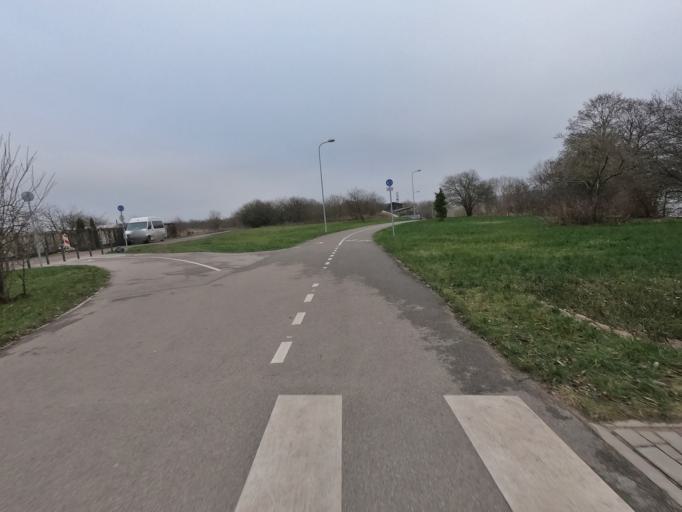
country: LV
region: Kekava
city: Kekava
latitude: 56.8804
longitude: 24.2186
